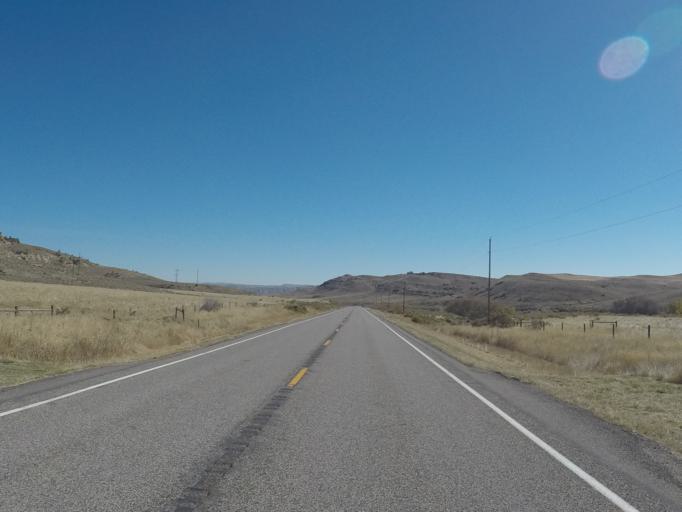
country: US
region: Montana
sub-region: Carbon County
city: Red Lodge
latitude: 45.1591
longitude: -109.0907
